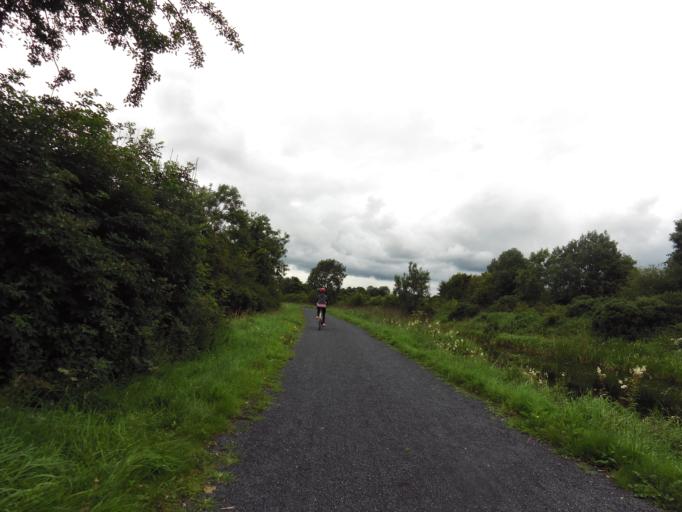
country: IE
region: Leinster
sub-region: An Iarmhi
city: An Muileann gCearr
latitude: 53.5132
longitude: -7.4254
